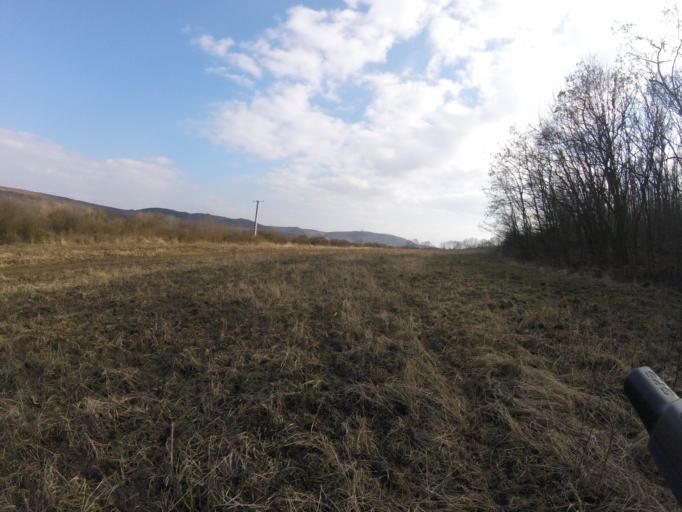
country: HU
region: Heves
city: Egerszalok
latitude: 47.8469
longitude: 20.3248
